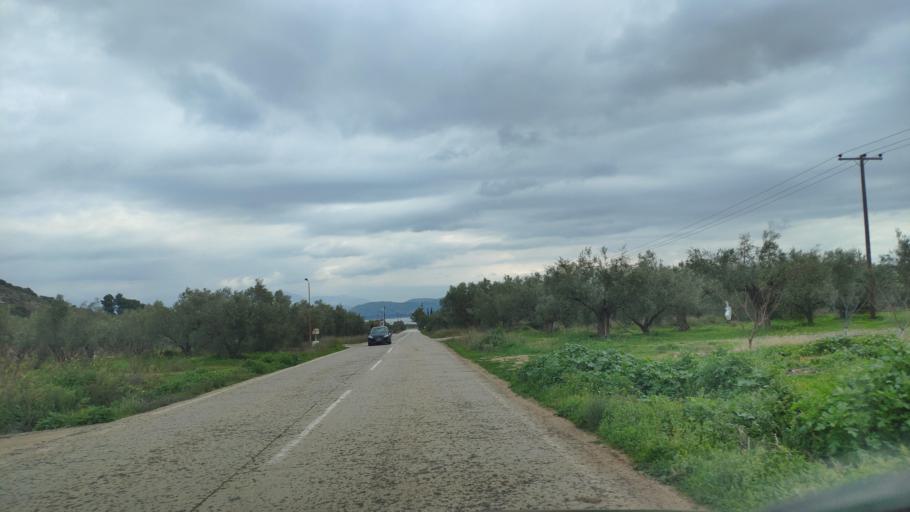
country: GR
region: Peloponnese
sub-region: Nomos Argolidos
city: Nea Kios
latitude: 37.5321
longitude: 22.7081
